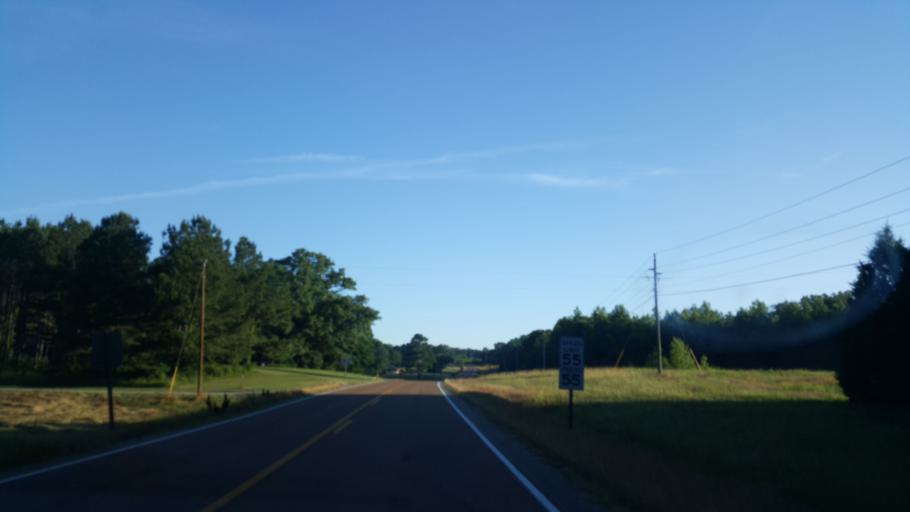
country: US
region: Tennessee
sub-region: McNairy County
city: Adamsville
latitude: 35.3272
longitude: -88.3554
